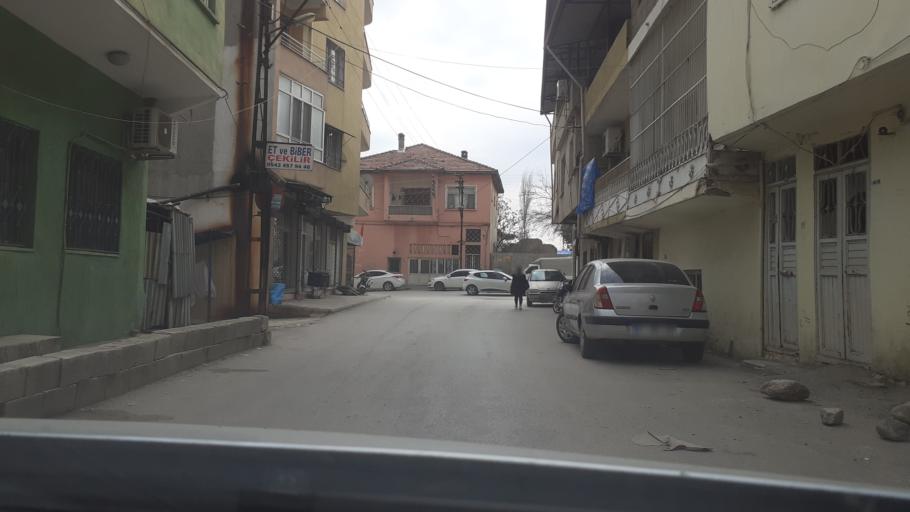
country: TR
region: Hatay
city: Kirikhan
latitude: 36.4969
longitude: 36.3538
